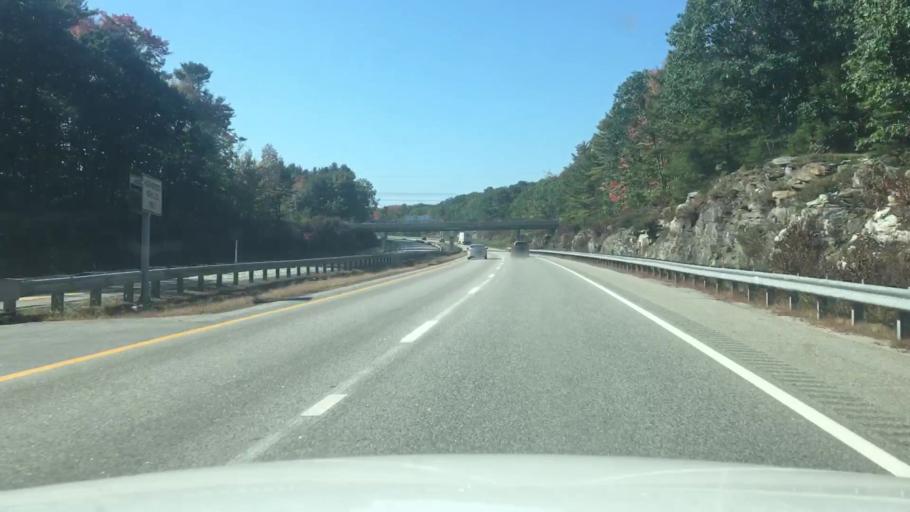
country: US
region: Maine
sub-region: Cumberland County
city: Falmouth
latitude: 43.7331
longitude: -70.2355
